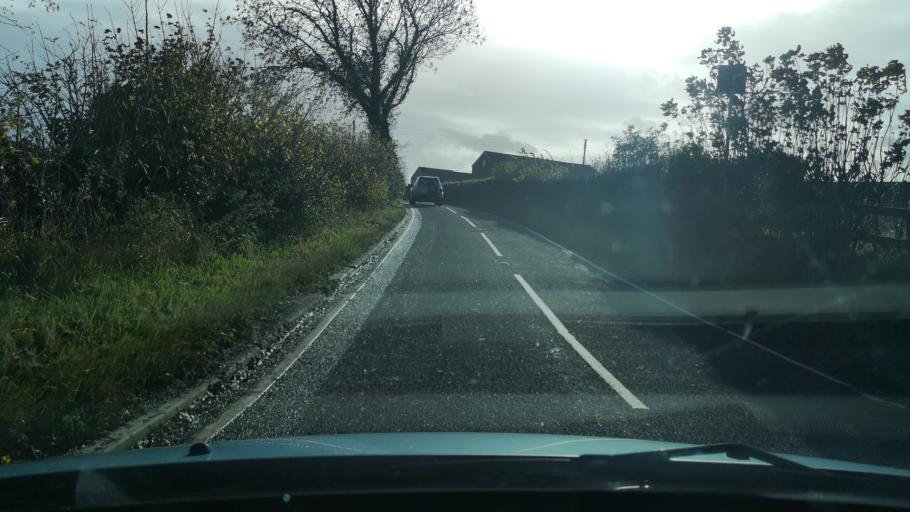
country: GB
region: England
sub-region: City and Borough of Wakefield
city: Ryhill
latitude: 53.6386
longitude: -1.4196
